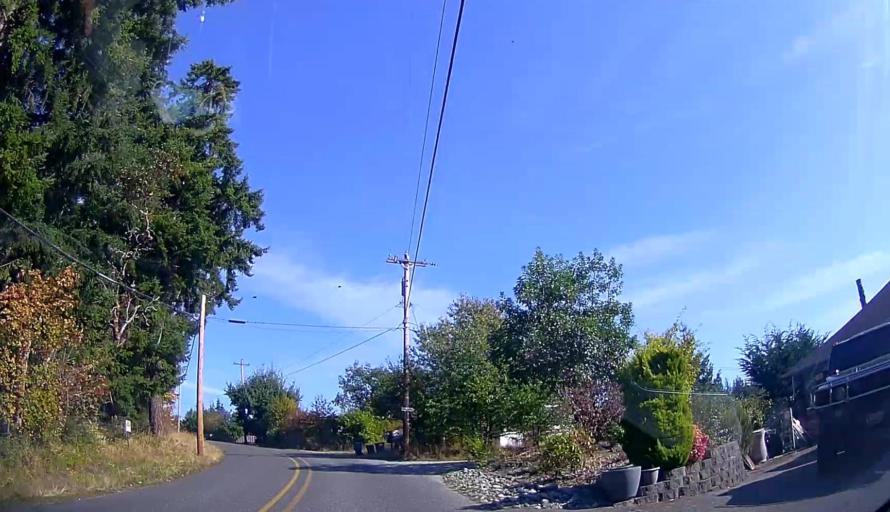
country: US
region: Washington
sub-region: Island County
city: Camano
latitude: 48.1753
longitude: -122.5252
